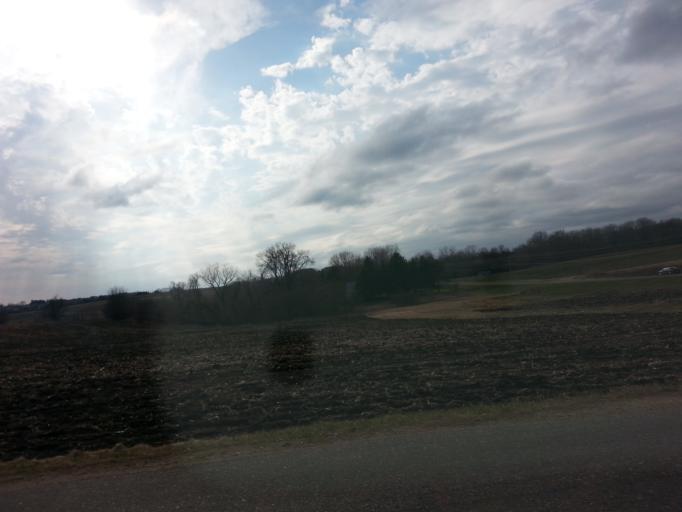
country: US
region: Wisconsin
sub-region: Pierce County
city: Ellsworth
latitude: 44.7497
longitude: -92.4668
